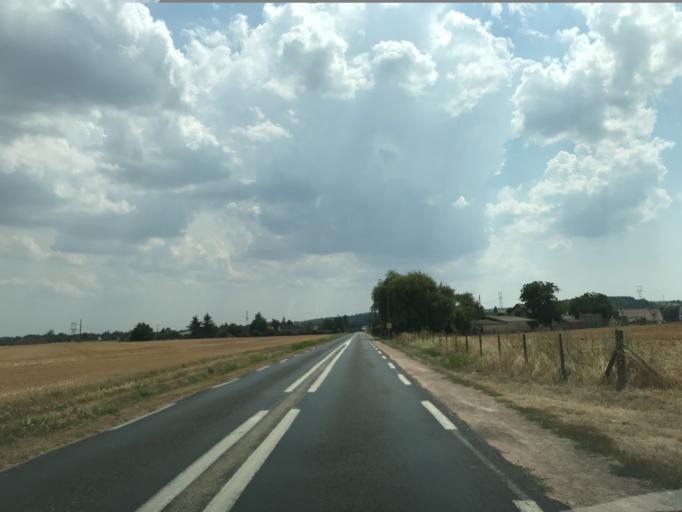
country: FR
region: Haute-Normandie
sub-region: Departement de l'Eure
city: Garennes-sur-Eure
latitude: 48.9209
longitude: 1.4433
